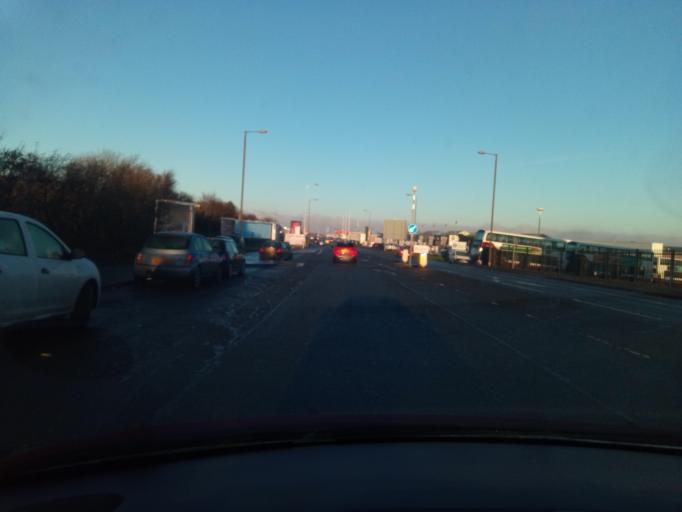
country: GB
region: Scotland
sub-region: West Lothian
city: Seafield
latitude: 55.9583
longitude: -3.1236
